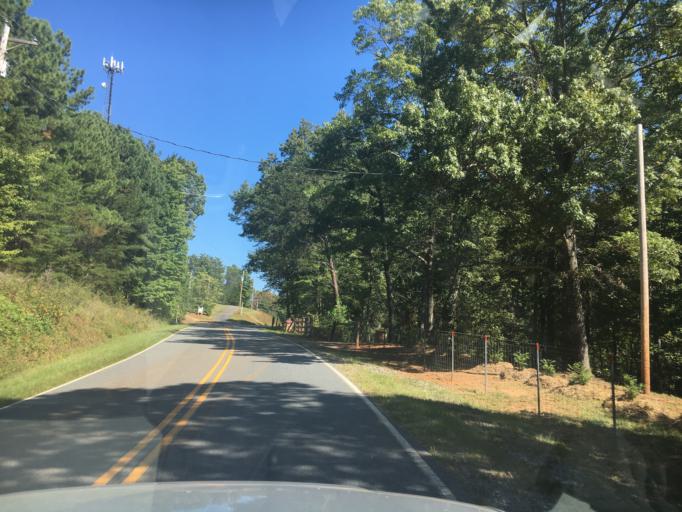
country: US
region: North Carolina
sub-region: Rutherford County
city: Lake Lure
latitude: 35.4068
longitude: -82.1725
